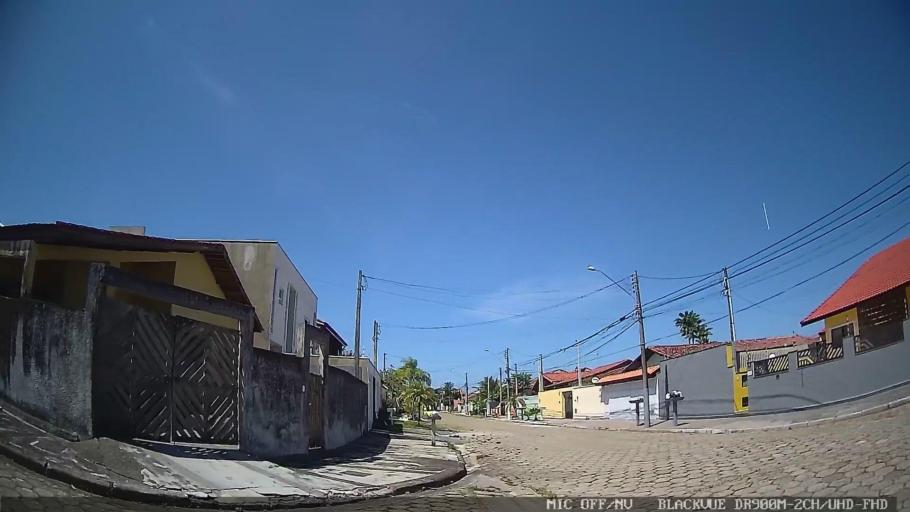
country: BR
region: Sao Paulo
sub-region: Peruibe
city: Peruibe
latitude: -24.2947
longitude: -46.9720
